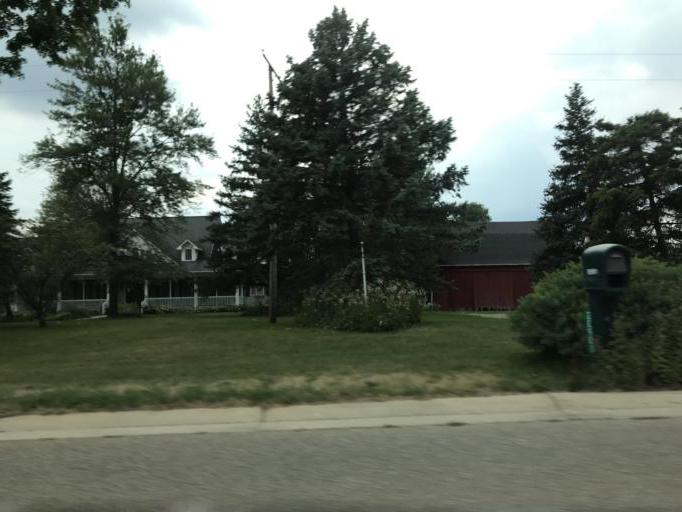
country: US
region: Michigan
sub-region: Wayne County
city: Northville
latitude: 42.4369
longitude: -83.5520
